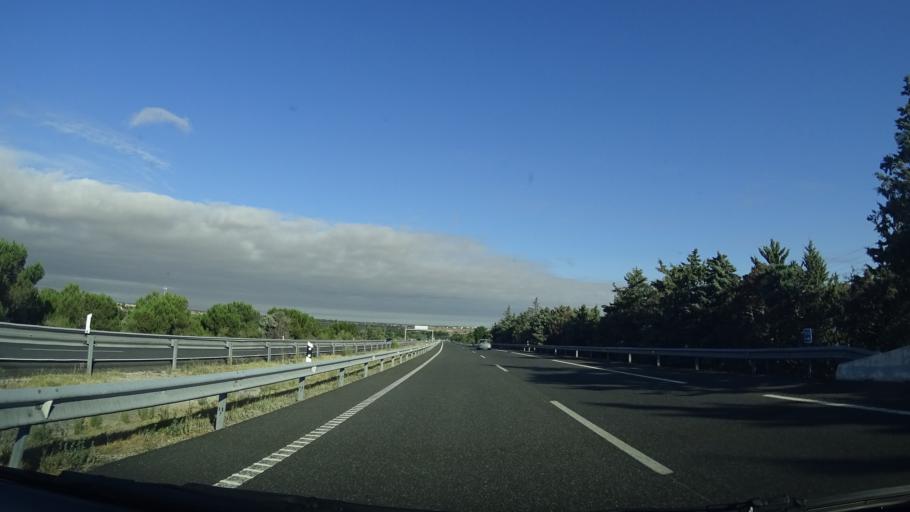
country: ES
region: Castille and Leon
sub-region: Provincia de Segovia
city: Labajos
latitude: 40.8562
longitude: -4.5491
